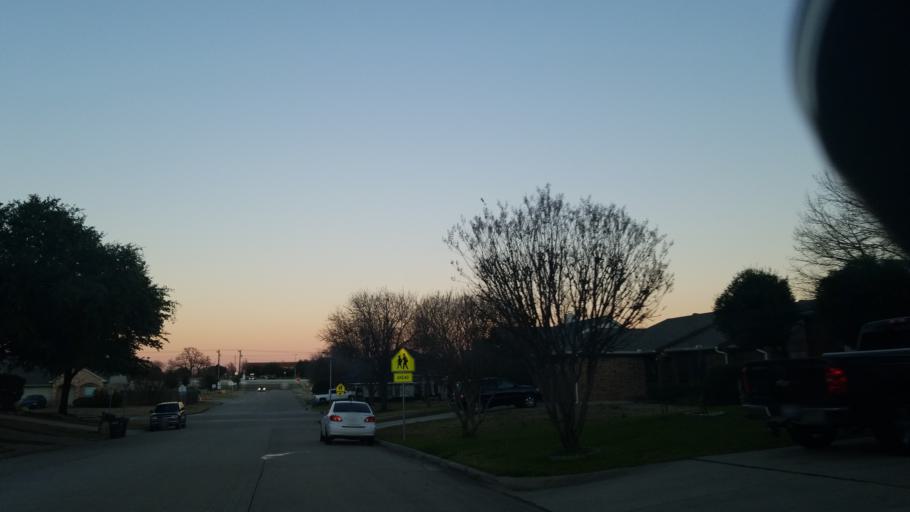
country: US
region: Texas
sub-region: Denton County
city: Hickory Creek
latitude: 33.1367
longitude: -97.0500
